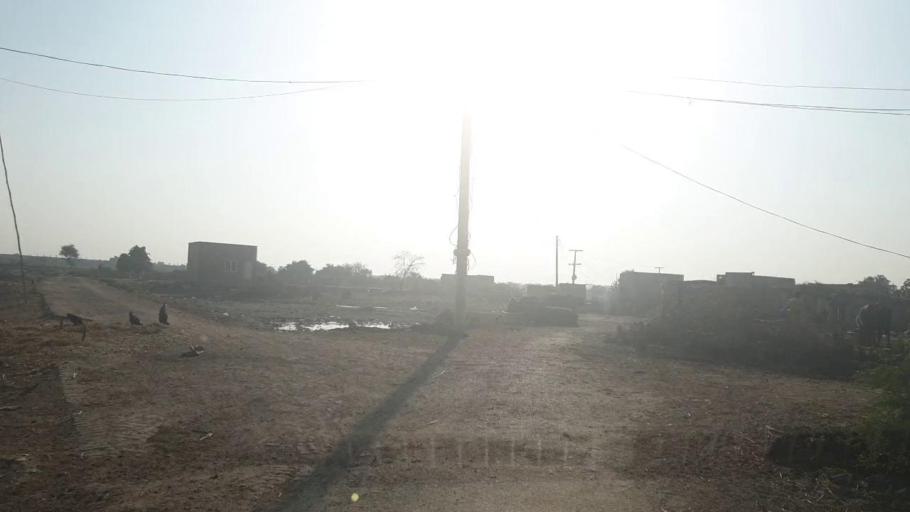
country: PK
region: Sindh
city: Jamshoro
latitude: 25.4084
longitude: 68.2934
